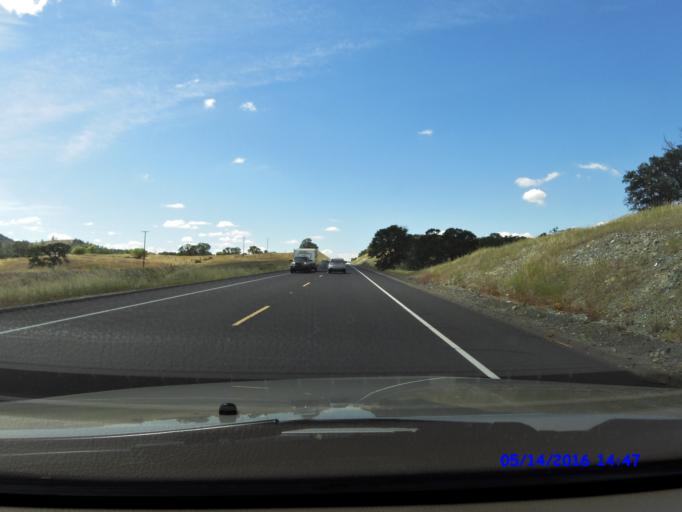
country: US
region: California
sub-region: Tuolumne County
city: Jamestown
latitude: 37.8536
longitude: -120.4149
